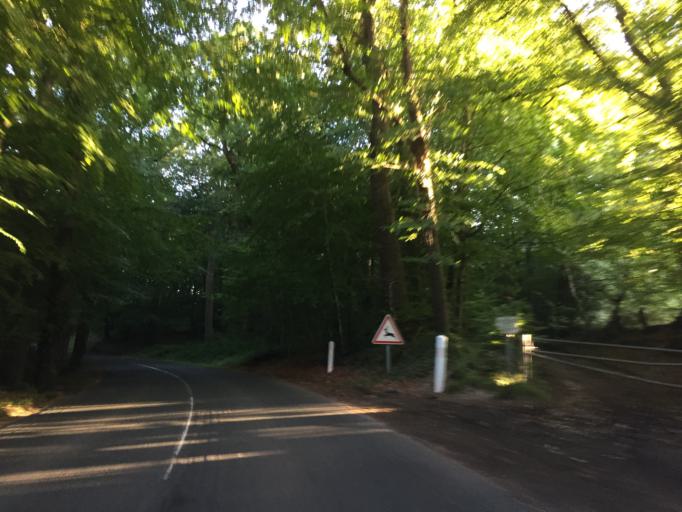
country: FR
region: Lower Normandy
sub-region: Departement du Calvados
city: Equemauville
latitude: 49.3964
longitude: 0.1937
